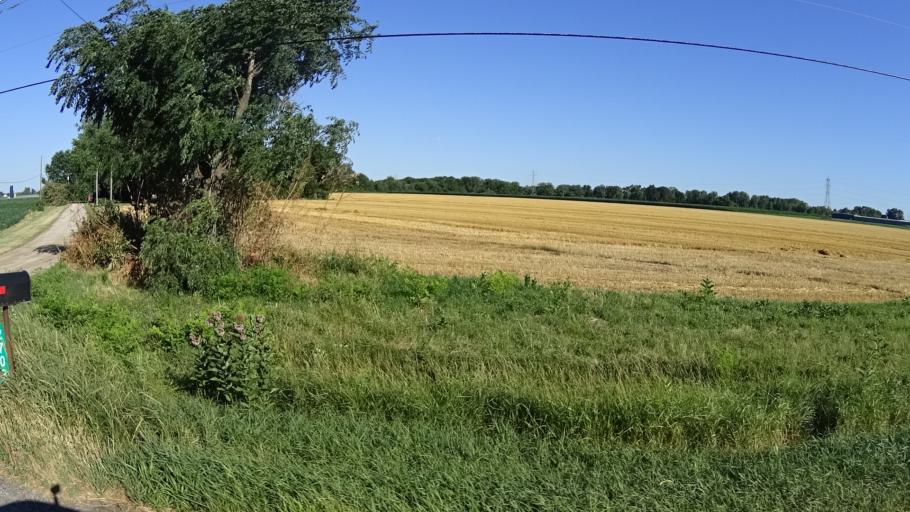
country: US
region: Ohio
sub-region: Erie County
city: Sandusky
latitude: 41.4297
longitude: -82.7462
